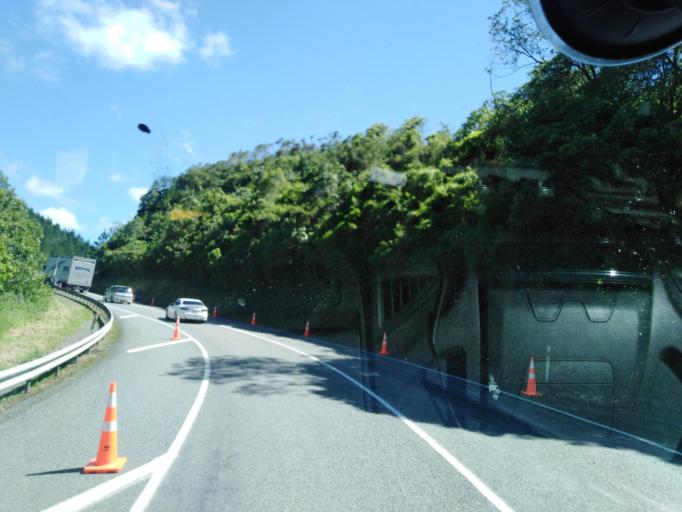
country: NZ
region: Nelson
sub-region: Nelson City
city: Nelson
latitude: -41.2027
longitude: 173.5632
